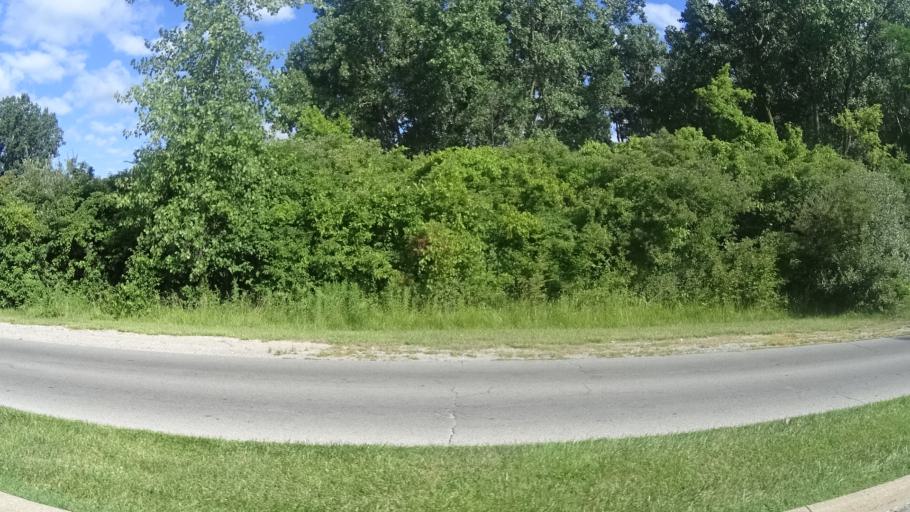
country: US
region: Ohio
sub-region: Erie County
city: Sandusky
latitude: 41.4231
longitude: -82.6671
